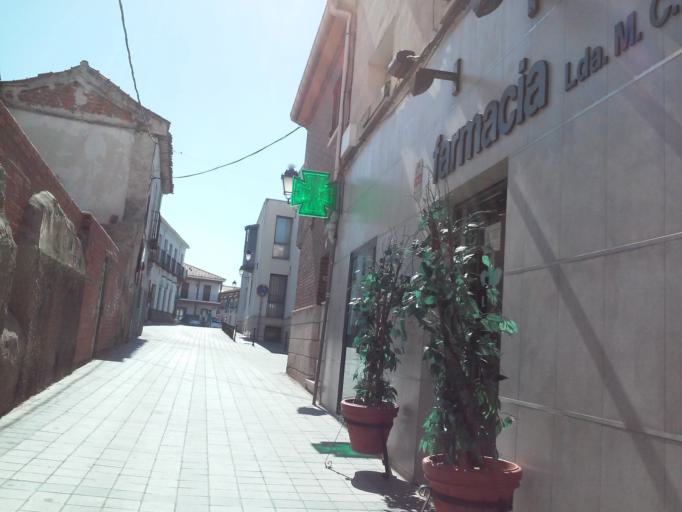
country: ES
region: Madrid
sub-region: Provincia de Madrid
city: Valdemoro
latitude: 40.1907
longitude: -3.6768
